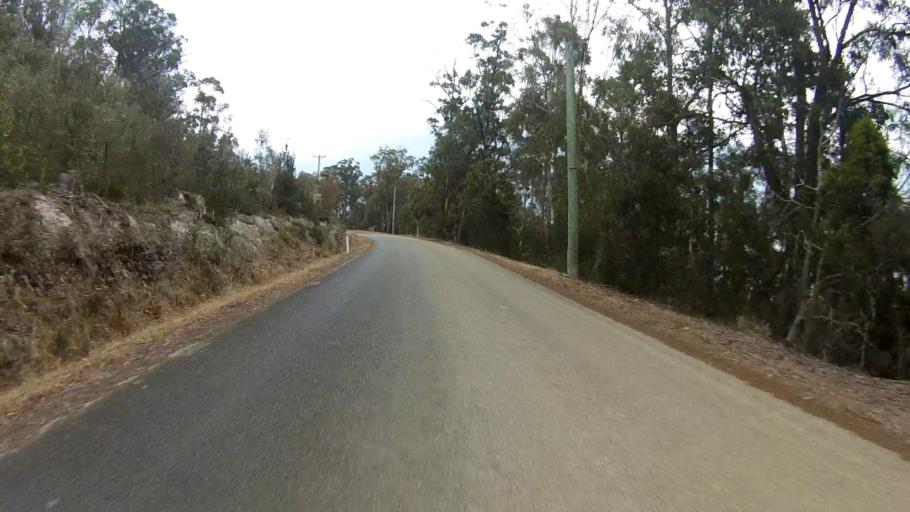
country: AU
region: Tasmania
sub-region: Huon Valley
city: Cygnet
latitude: -43.2187
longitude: 147.0930
